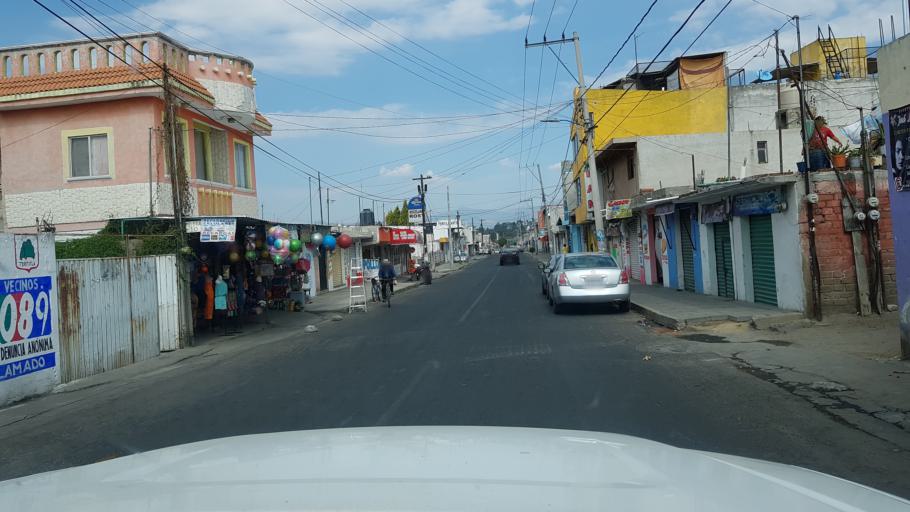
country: MX
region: Puebla
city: Tepetitla
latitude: 19.2921
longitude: -98.4018
